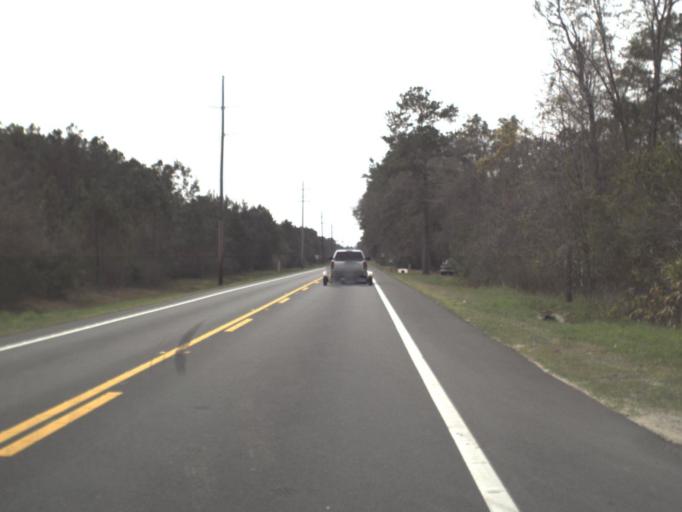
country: US
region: Florida
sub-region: Gadsden County
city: Midway
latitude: 30.3924
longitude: -84.6194
